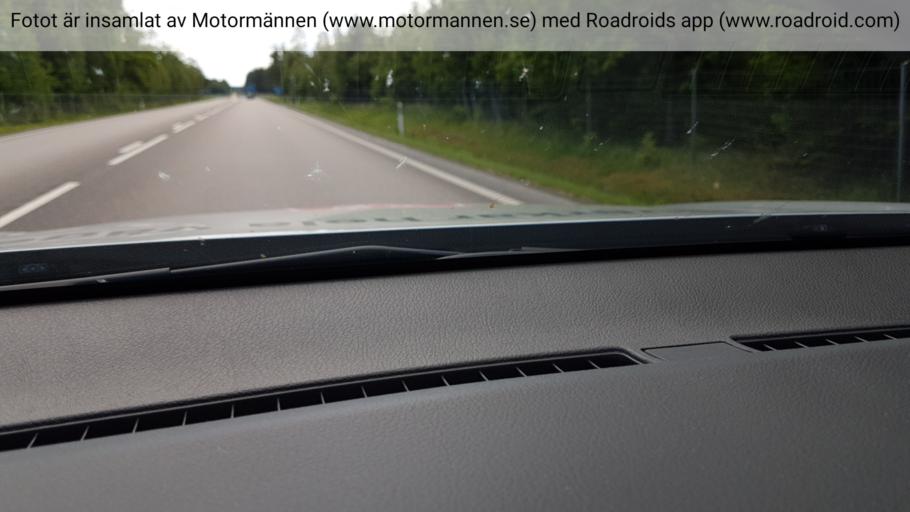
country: SE
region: Vaestra Goetaland
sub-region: Lidkopings Kommun
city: Vinninga
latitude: 58.4654
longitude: 13.2199
